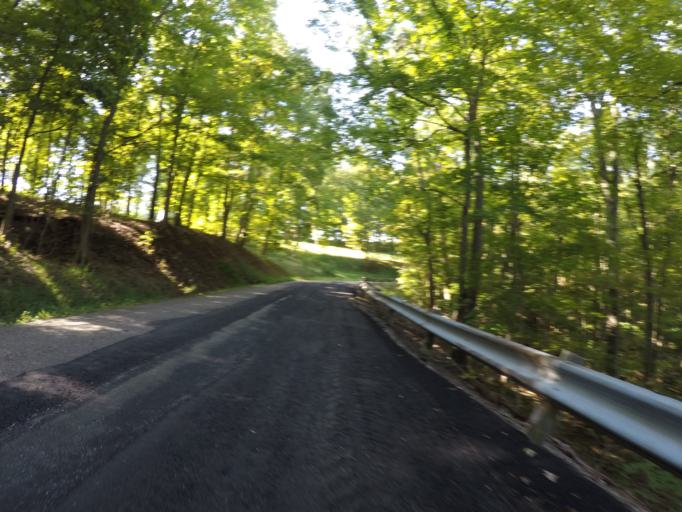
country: US
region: West Virginia
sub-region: Cabell County
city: Huntington
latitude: 38.4678
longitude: -82.4605
